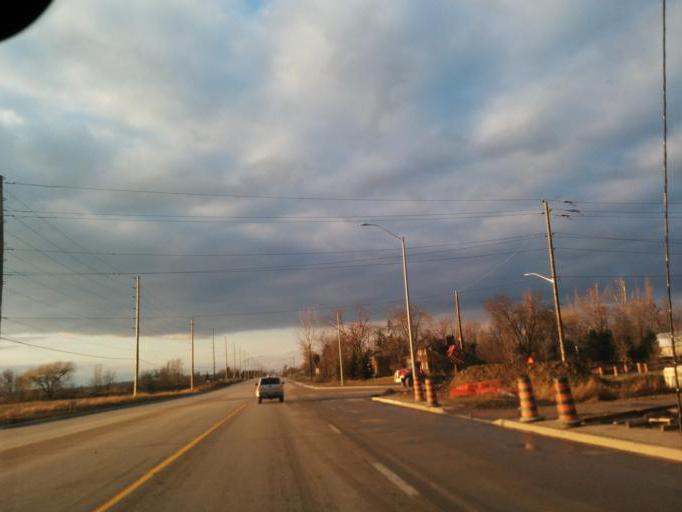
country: CA
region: Ontario
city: Brampton
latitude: 43.8474
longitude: -79.7173
